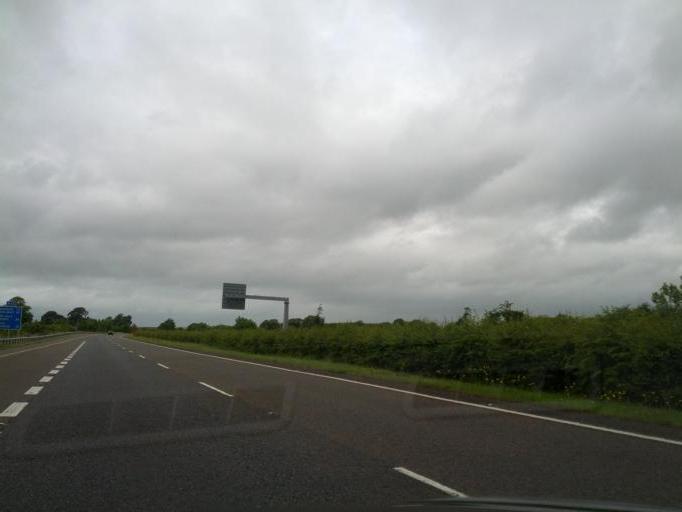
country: IE
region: Munster
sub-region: An Clar
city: Newmarket on Fergus
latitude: 52.7547
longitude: -8.9090
